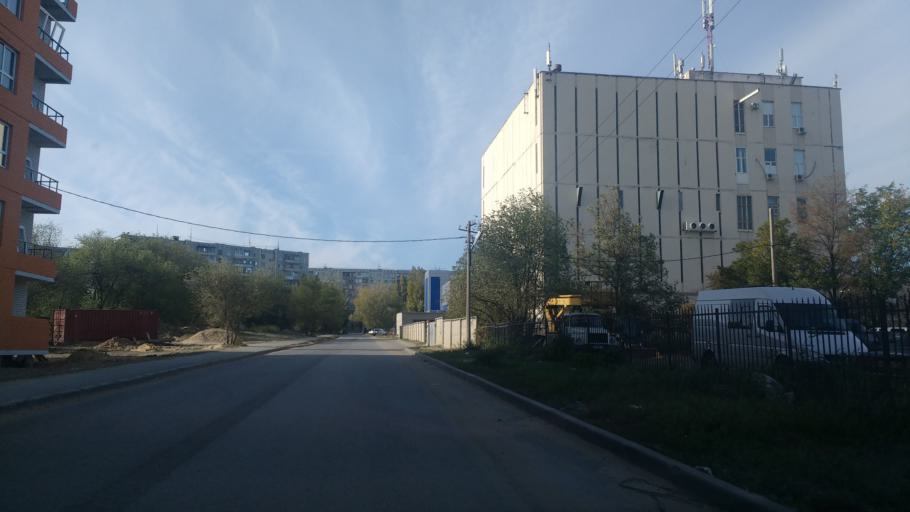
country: RU
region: Volgograd
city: Krasnoslobodsk
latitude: 48.7642
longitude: 44.5508
